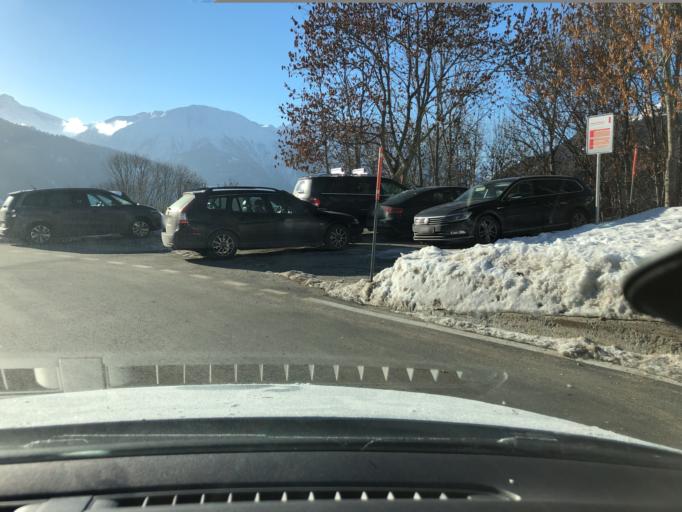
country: CH
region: Valais
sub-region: Goms District
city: Fiesch
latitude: 46.4336
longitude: 8.1468
